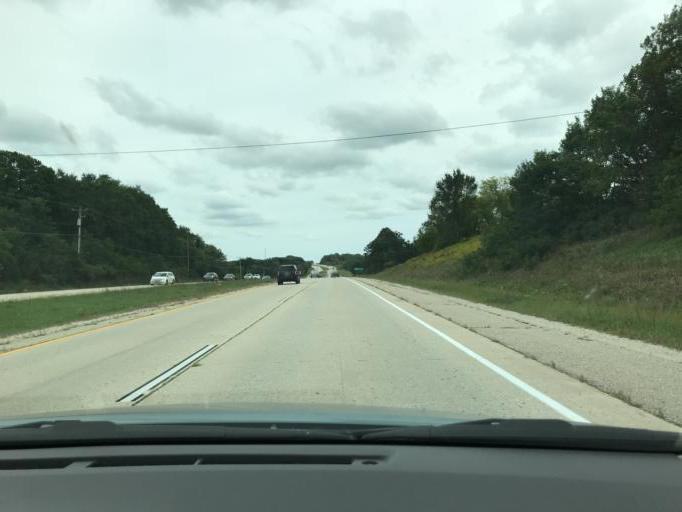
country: US
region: Wisconsin
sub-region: Kenosha County
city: Bristol
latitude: 42.5680
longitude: -88.0756
